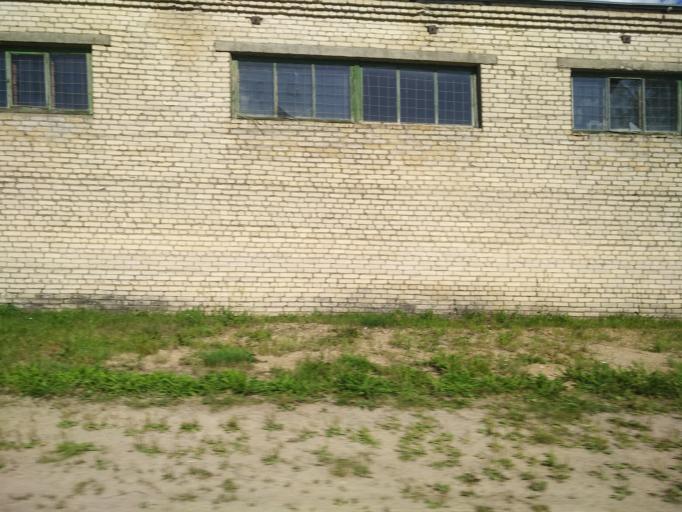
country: BY
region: Vitebsk
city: Mosar
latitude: 55.1254
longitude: 27.2107
